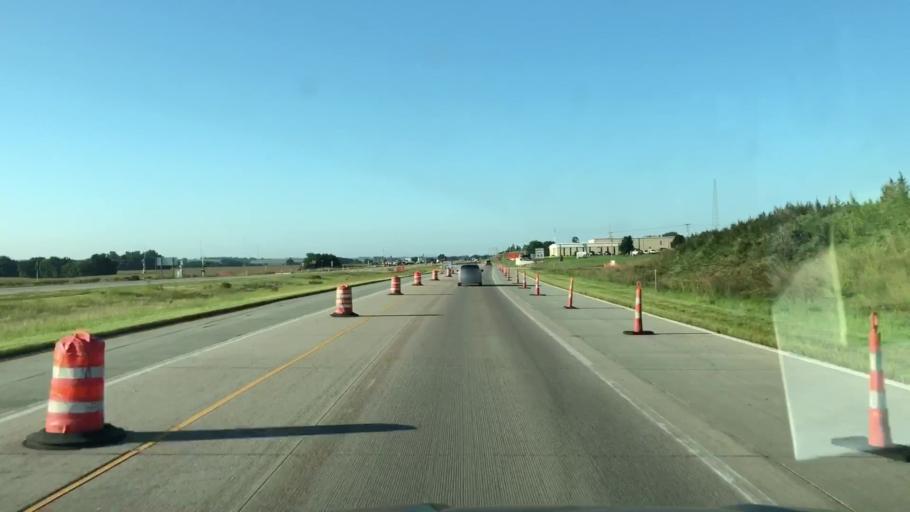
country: US
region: Iowa
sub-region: Plymouth County
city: Le Mars
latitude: 42.7517
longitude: -96.2107
